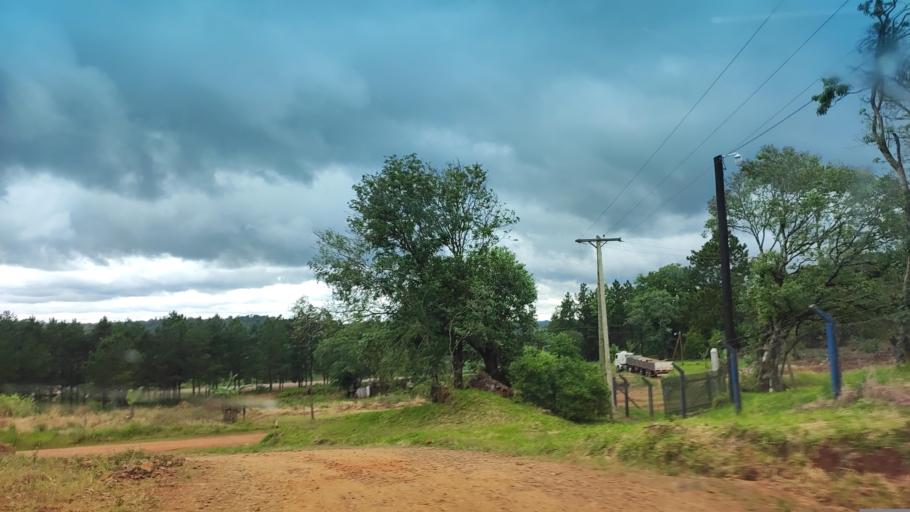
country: AR
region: Misiones
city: Dos de Mayo
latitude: -27.0113
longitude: -54.6199
